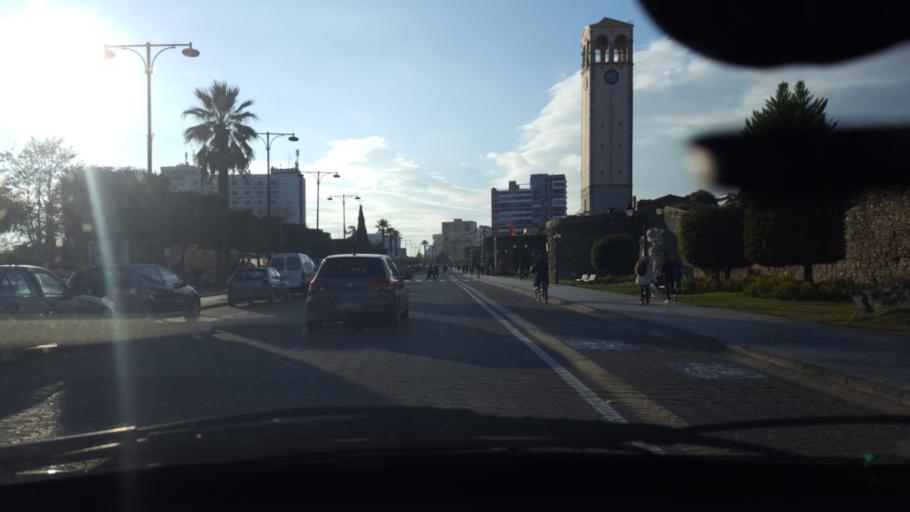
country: AL
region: Elbasan
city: Elbasan
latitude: 41.1133
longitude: 20.0832
